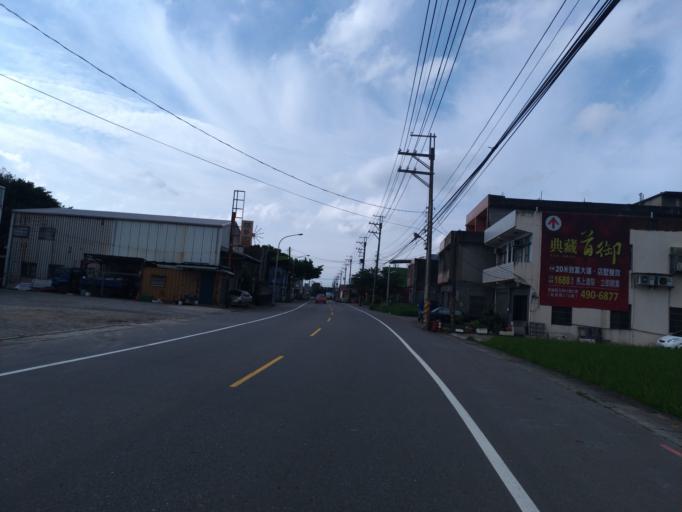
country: TW
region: Taiwan
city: Daxi
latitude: 24.9354
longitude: 121.1693
